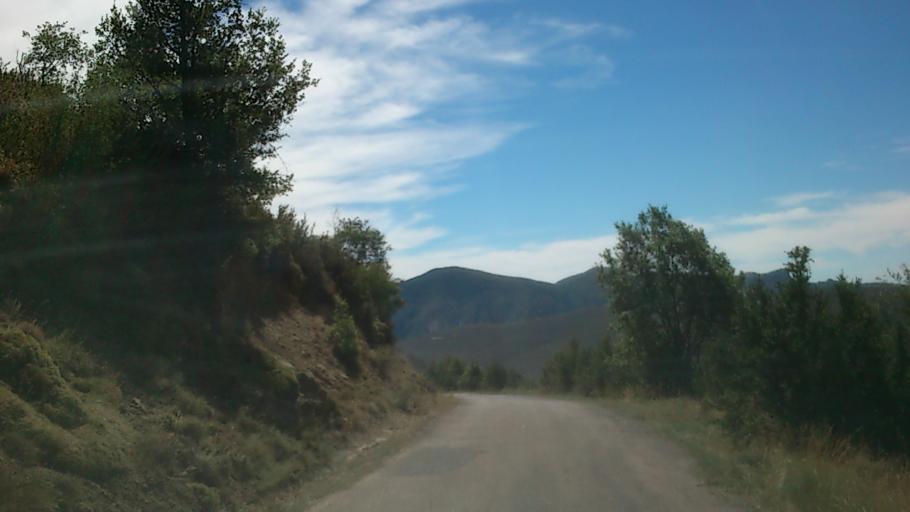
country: ES
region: Aragon
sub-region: Provincia de Huesca
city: Arguis
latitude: 42.3261
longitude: -0.3985
